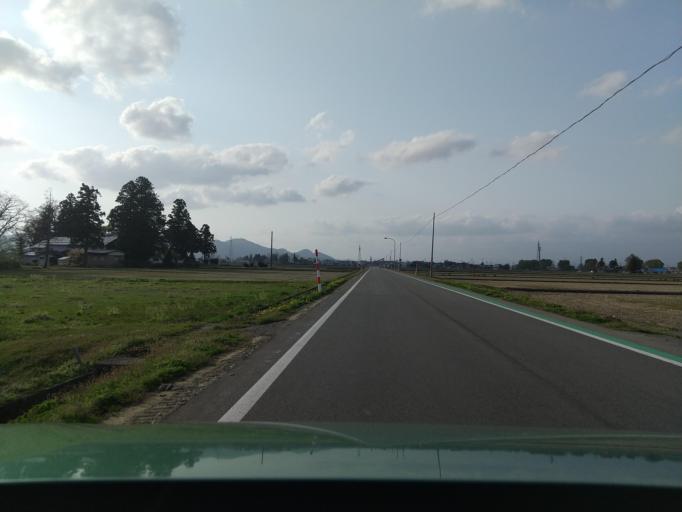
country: JP
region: Akita
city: Omagari
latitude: 39.4201
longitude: 140.4919
